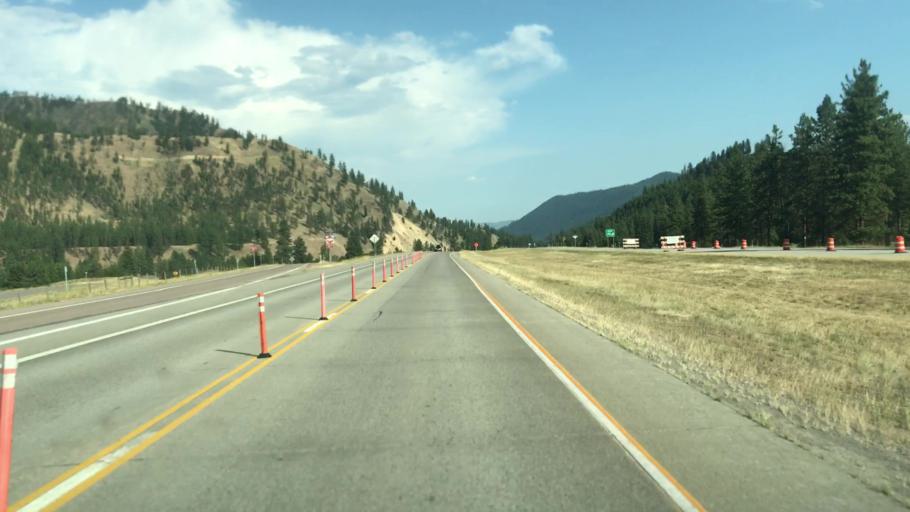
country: US
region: Montana
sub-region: Mineral County
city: Superior
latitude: 47.2283
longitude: -114.9733
